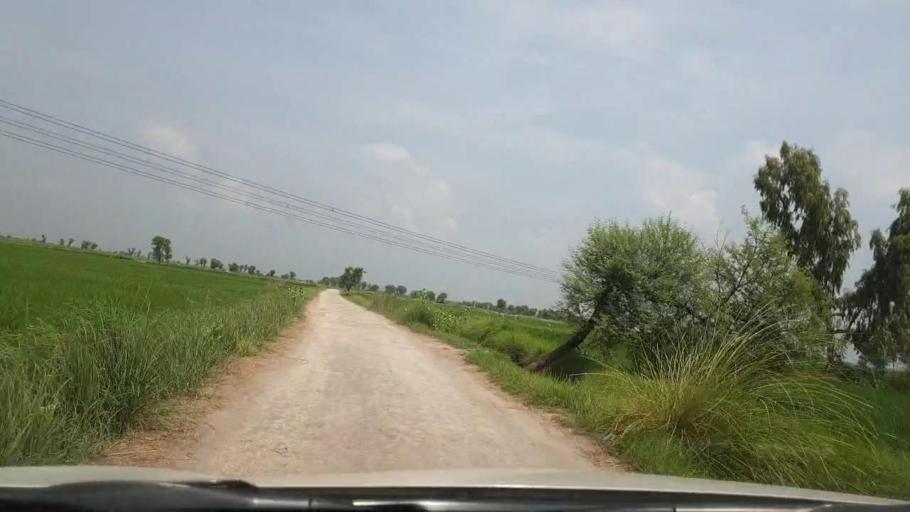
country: PK
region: Sindh
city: Dokri
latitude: 27.3905
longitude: 68.0550
